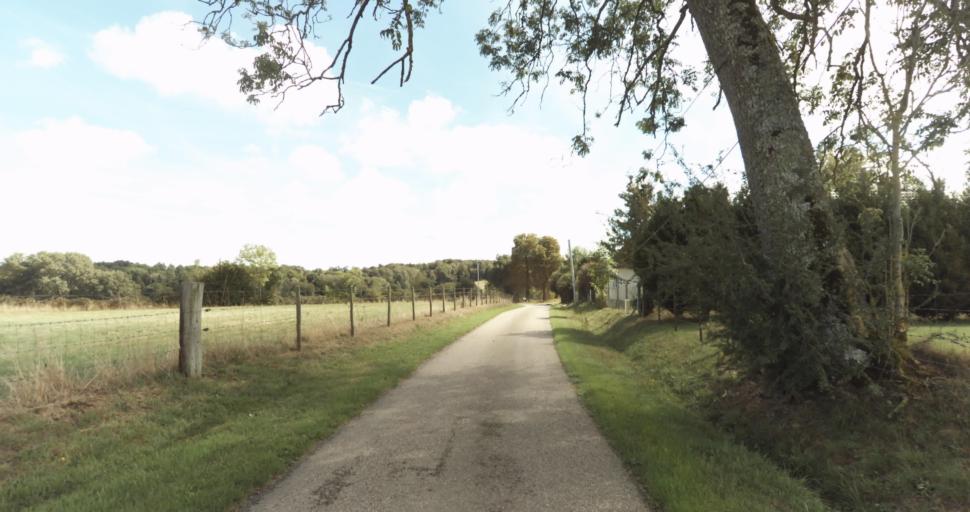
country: FR
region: Lower Normandy
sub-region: Departement du Calvados
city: Orbec
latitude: 48.9151
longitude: 0.3801
